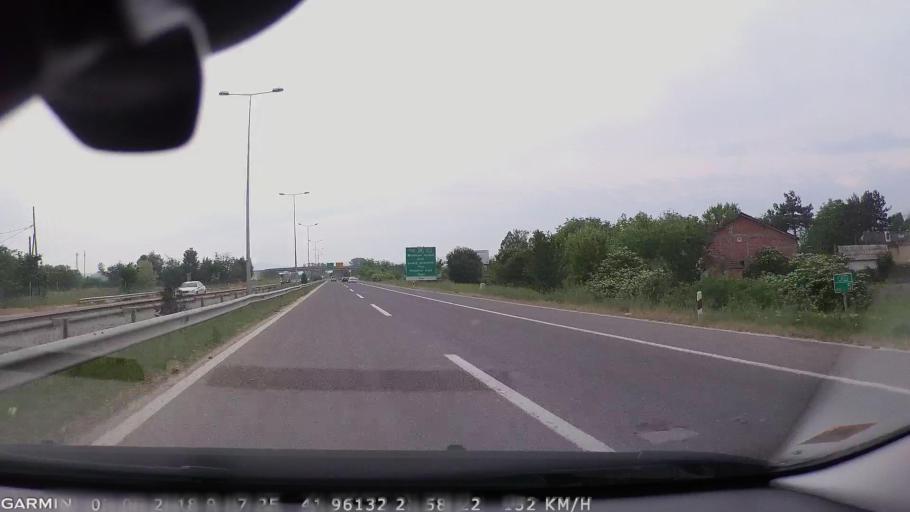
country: MK
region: Ilinden
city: Idrizovo
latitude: 41.9702
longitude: 21.5689
